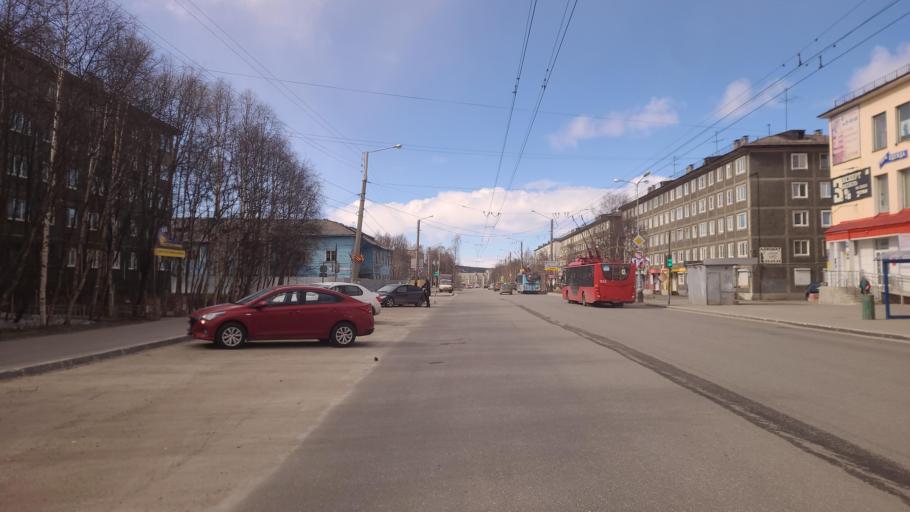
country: RU
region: Murmansk
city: Murmansk
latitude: 68.9517
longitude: 33.0739
